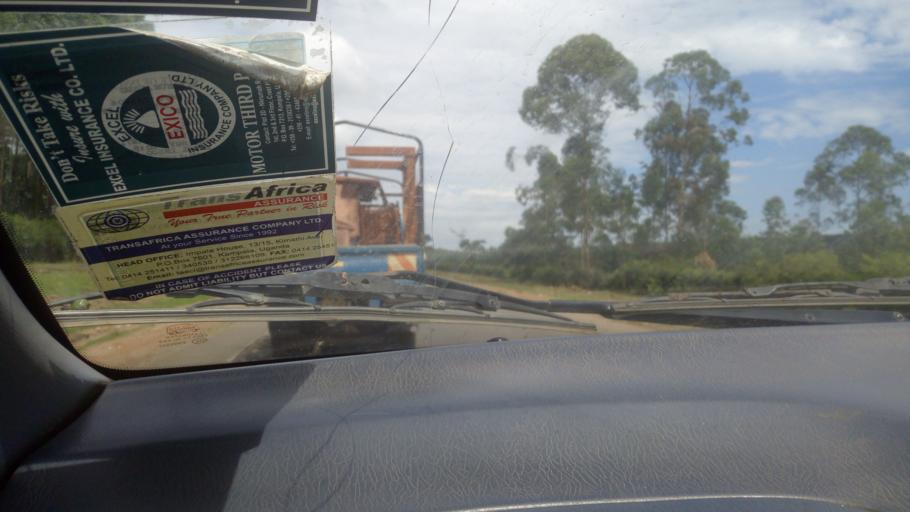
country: UG
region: Western Region
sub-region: Mbarara District
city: Bwizibwera
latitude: -0.4189
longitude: 30.5697
